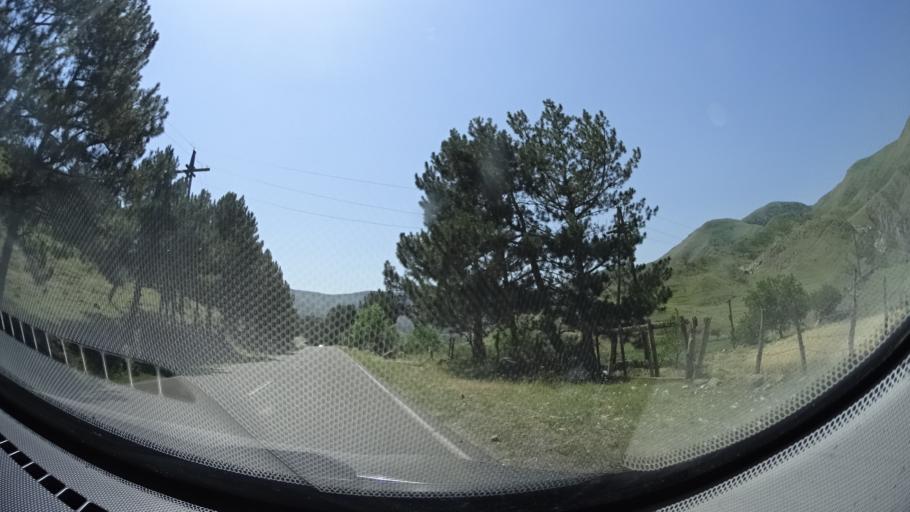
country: GE
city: Akhalk'alak'i
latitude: 41.4242
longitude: 43.3212
